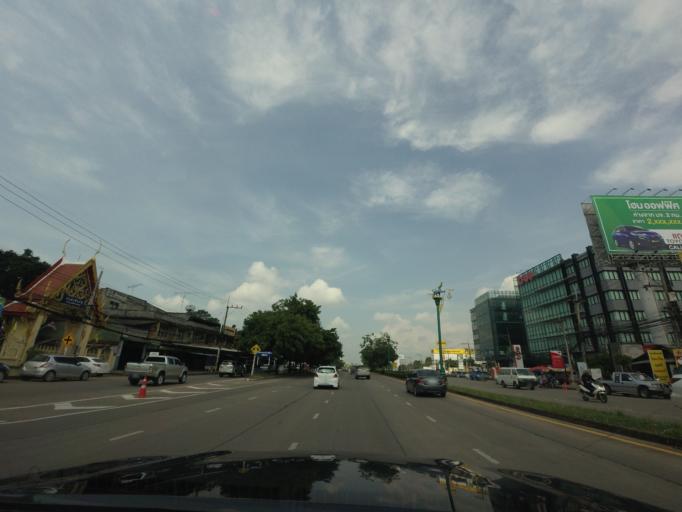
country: TH
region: Khon Kaen
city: Khon Kaen
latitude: 16.4404
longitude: 102.8223
